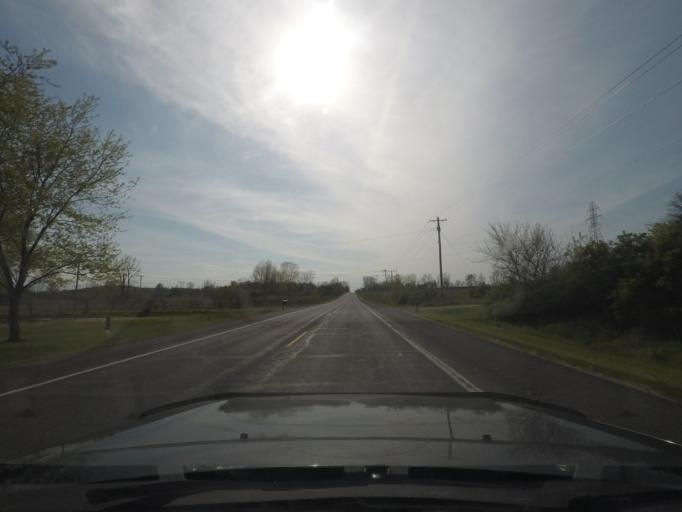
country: US
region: Indiana
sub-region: LaPorte County
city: Hudson Lake
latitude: 41.7981
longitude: -86.5141
